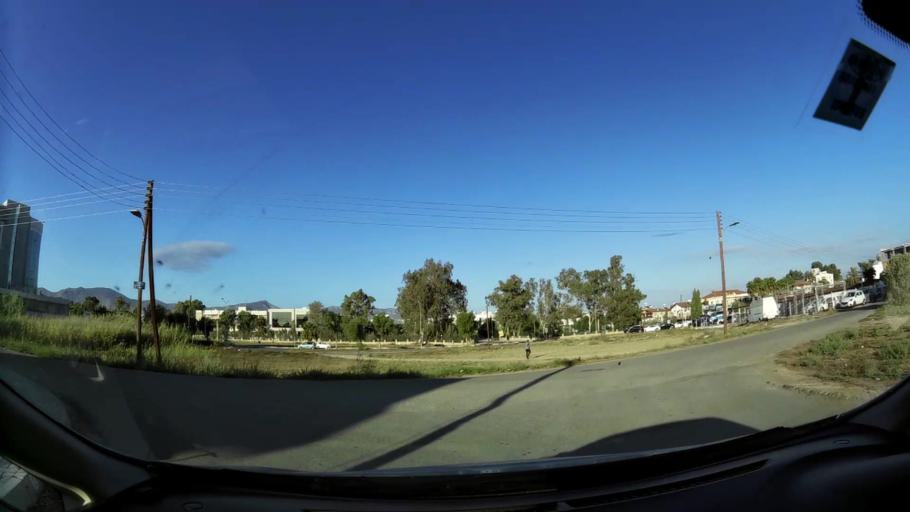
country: CY
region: Lefkosia
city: Nicosia
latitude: 35.2012
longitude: 33.3354
